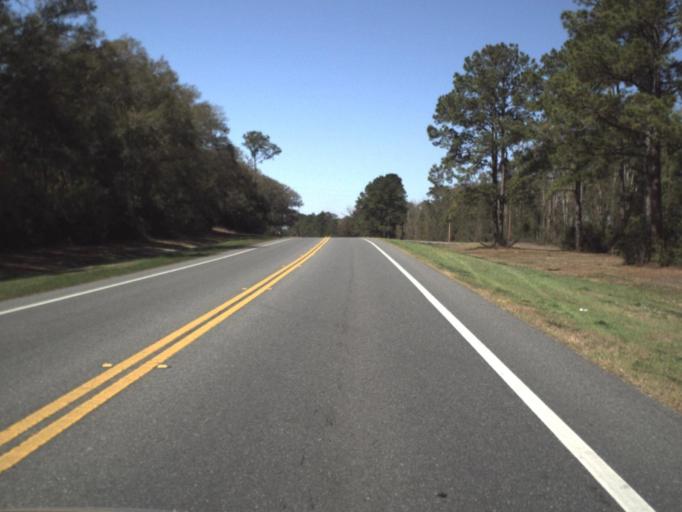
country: US
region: Florida
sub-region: Jackson County
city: Marianna
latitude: 30.7348
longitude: -85.1005
